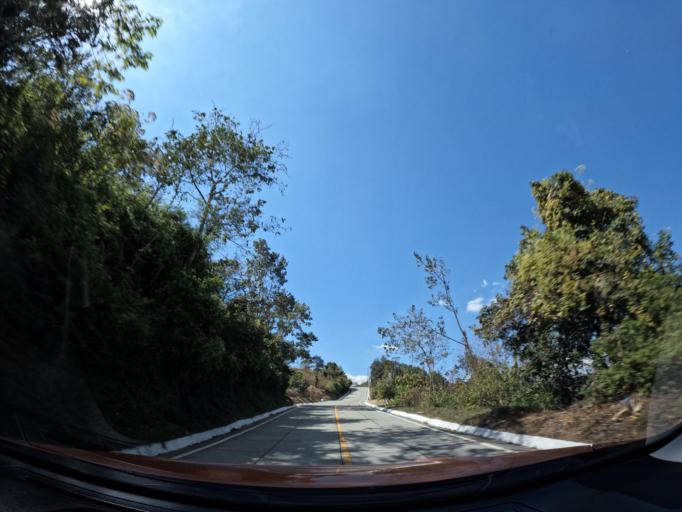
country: GT
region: Solola
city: San Antonio Palopo
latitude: 14.6926
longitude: -91.0738
